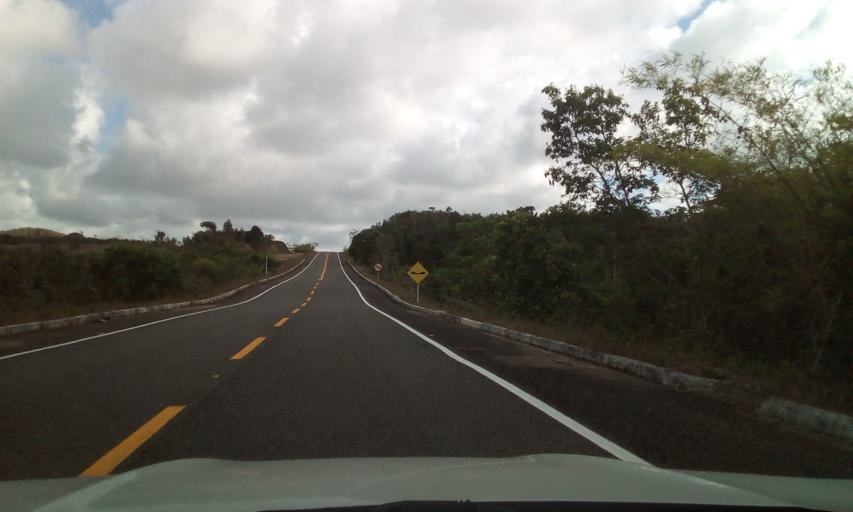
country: BR
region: Bahia
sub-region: Conde
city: Conde
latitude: -11.6748
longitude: -37.5624
